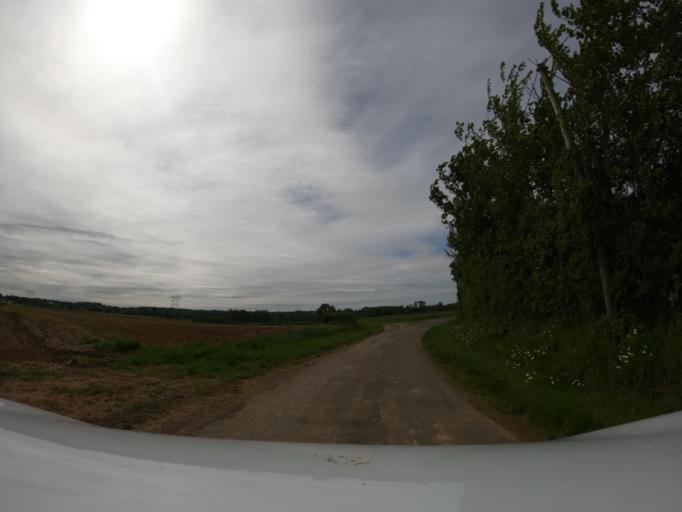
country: FR
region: Pays de la Loire
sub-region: Departement de la Vendee
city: Saint-Hilaire-des-Loges
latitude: 46.4997
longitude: -0.6565
